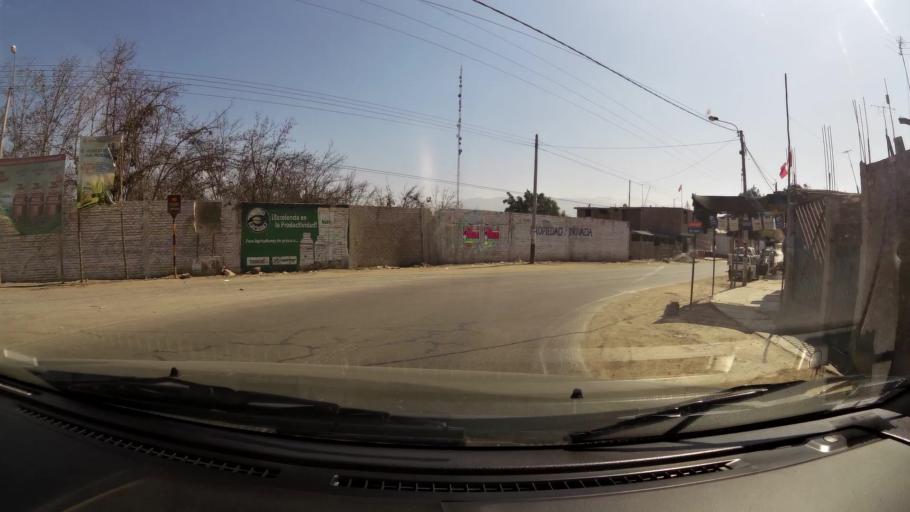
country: PE
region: Ica
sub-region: Provincia de Ica
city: San Juan Bautista
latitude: -13.9800
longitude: -75.6981
